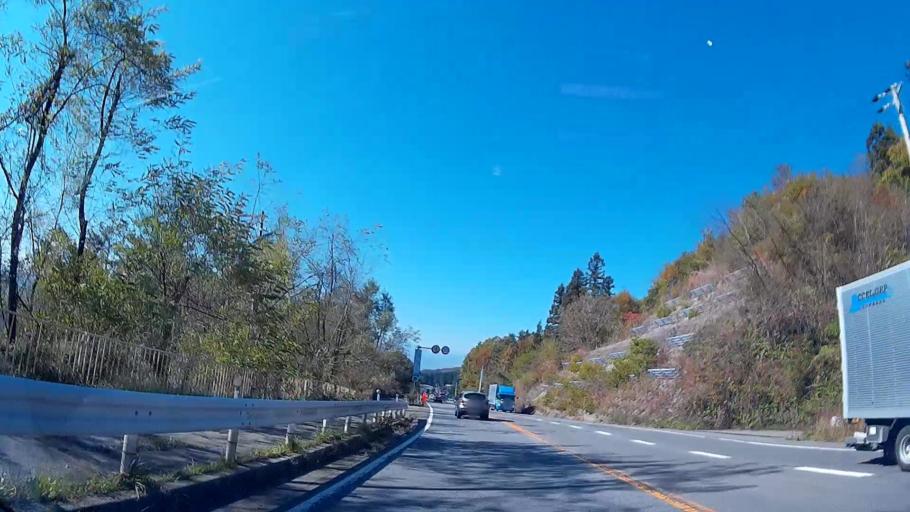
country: JP
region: Nagano
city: Okaya
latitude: 36.0911
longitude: 138.0235
